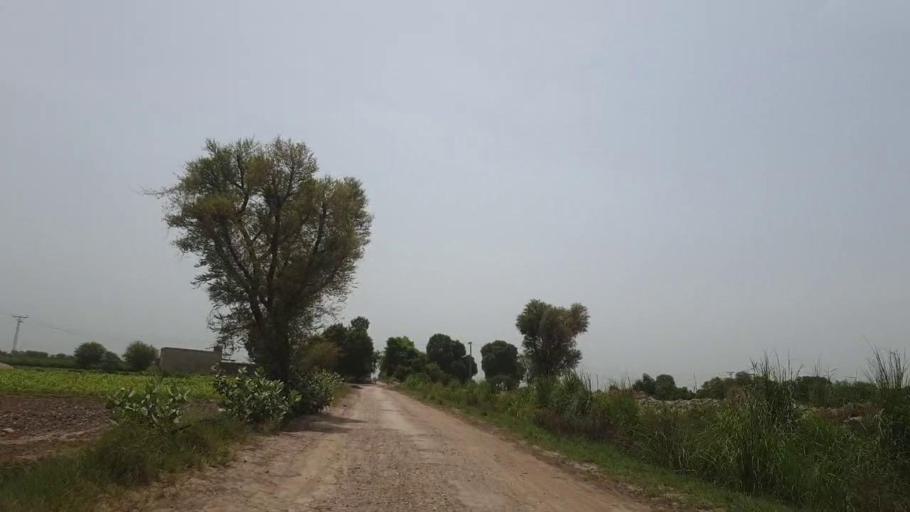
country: PK
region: Sindh
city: Sakrand
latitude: 26.0750
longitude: 68.2652
